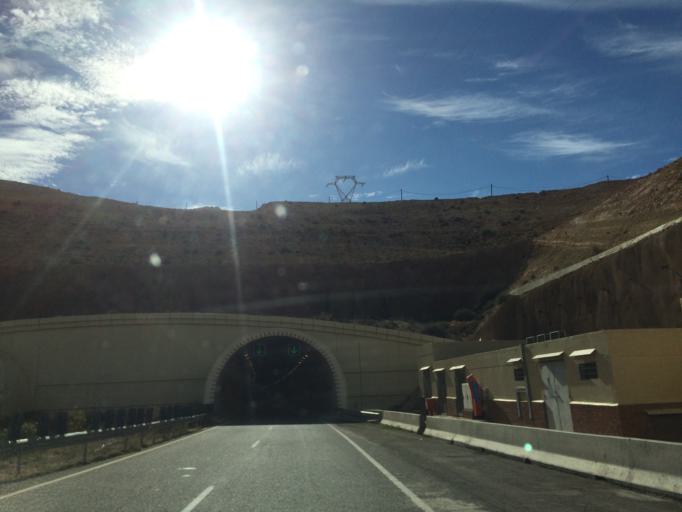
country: MA
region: Marrakech-Tensift-Al Haouz
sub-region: Chichaoua
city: Taouloukoult
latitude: 31.1923
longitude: -8.9806
